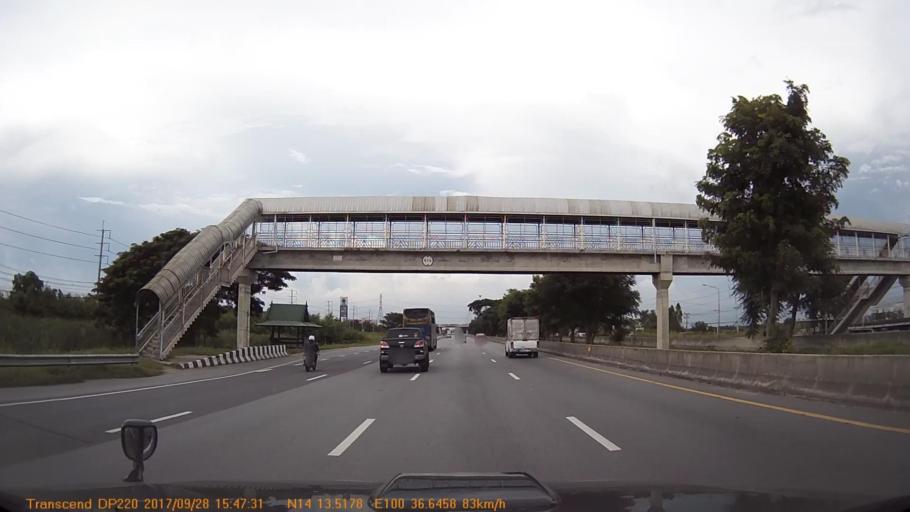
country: TH
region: Phra Nakhon Si Ayutthaya
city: Bang Pa-in
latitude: 14.2251
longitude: 100.6107
